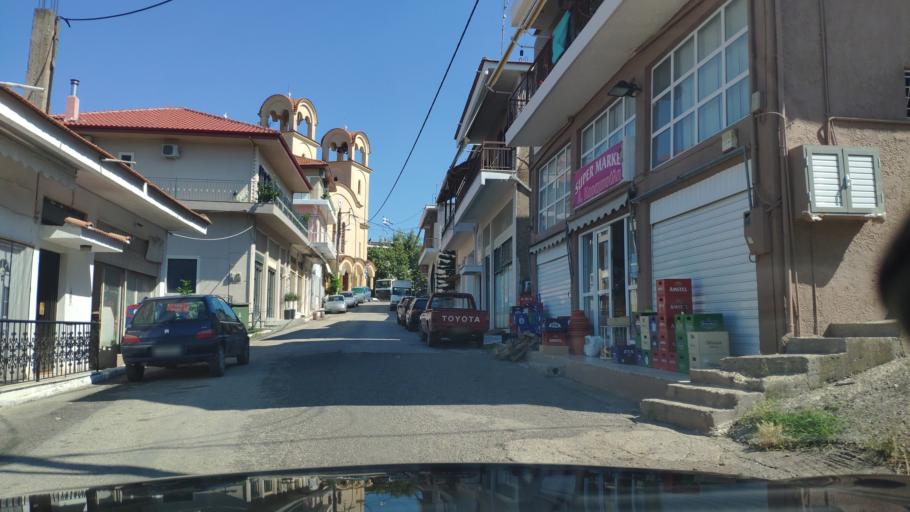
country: GR
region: West Greece
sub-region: Nomos Aitolias kai Akarnanias
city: Katouna
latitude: 38.7864
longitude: 21.1160
